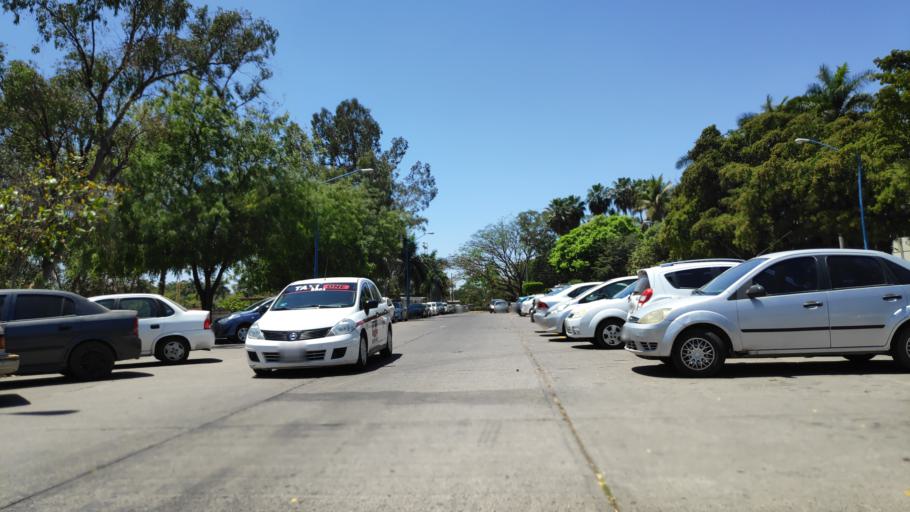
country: MX
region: Sinaloa
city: Culiacan
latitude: 24.8255
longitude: -107.3818
